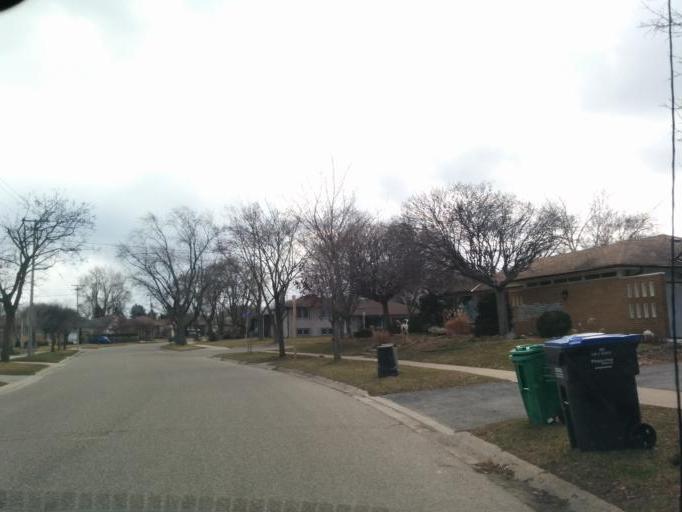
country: CA
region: Ontario
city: Etobicoke
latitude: 43.6028
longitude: -79.5683
